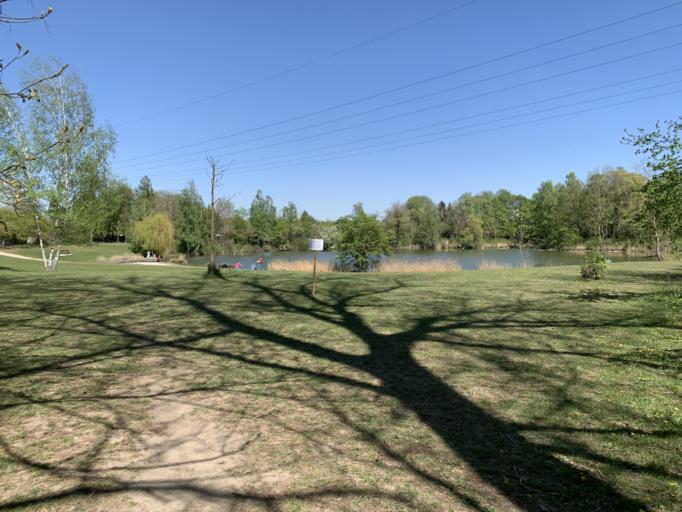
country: DE
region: Bavaria
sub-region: Swabia
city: Gersthofen
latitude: 48.4227
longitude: 10.8914
